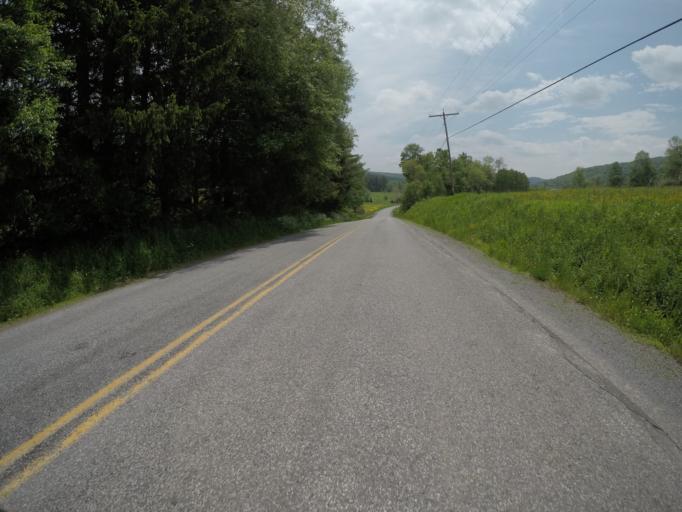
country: US
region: New York
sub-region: Delaware County
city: Stamford
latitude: 42.2076
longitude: -74.6797
